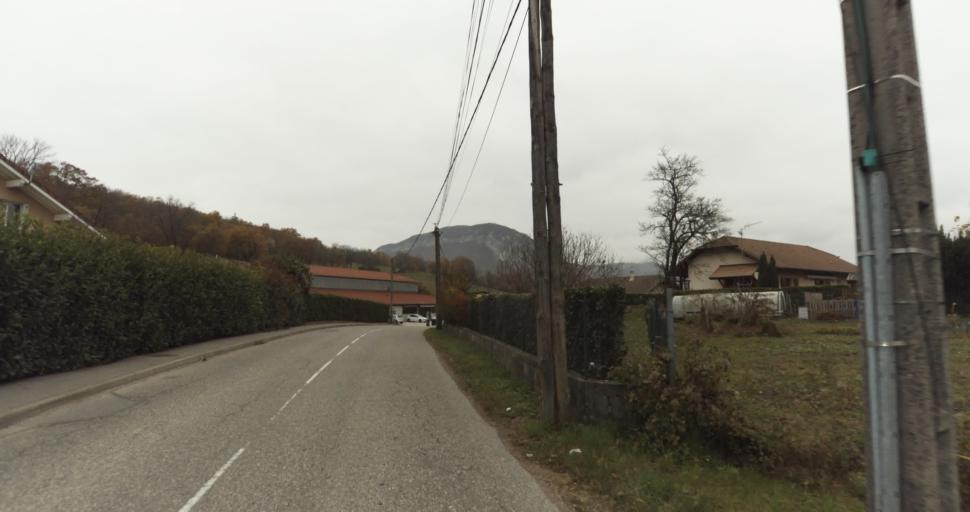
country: FR
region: Rhone-Alpes
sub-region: Departement de la Haute-Savoie
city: Poisy
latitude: 45.9324
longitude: 6.0625
